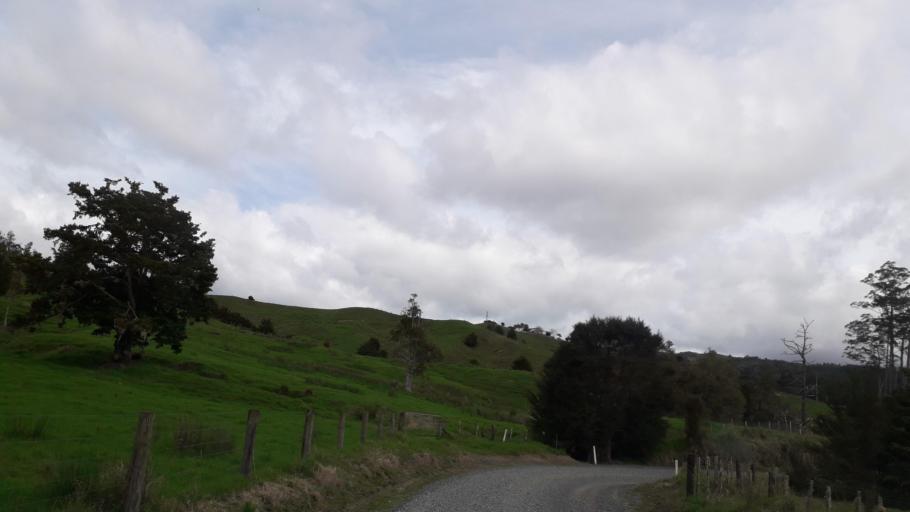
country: NZ
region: Northland
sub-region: Far North District
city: Waimate North
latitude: -35.1543
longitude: 173.7158
